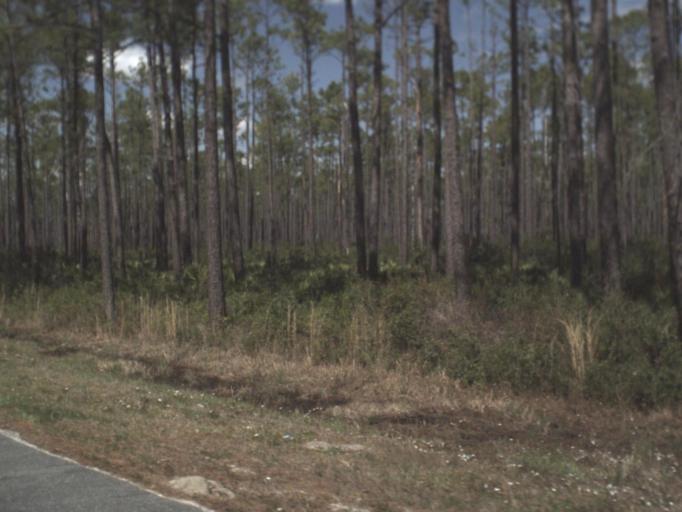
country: US
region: Florida
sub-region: Gadsden County
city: Midway
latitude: 30.3344
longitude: -84.4780
